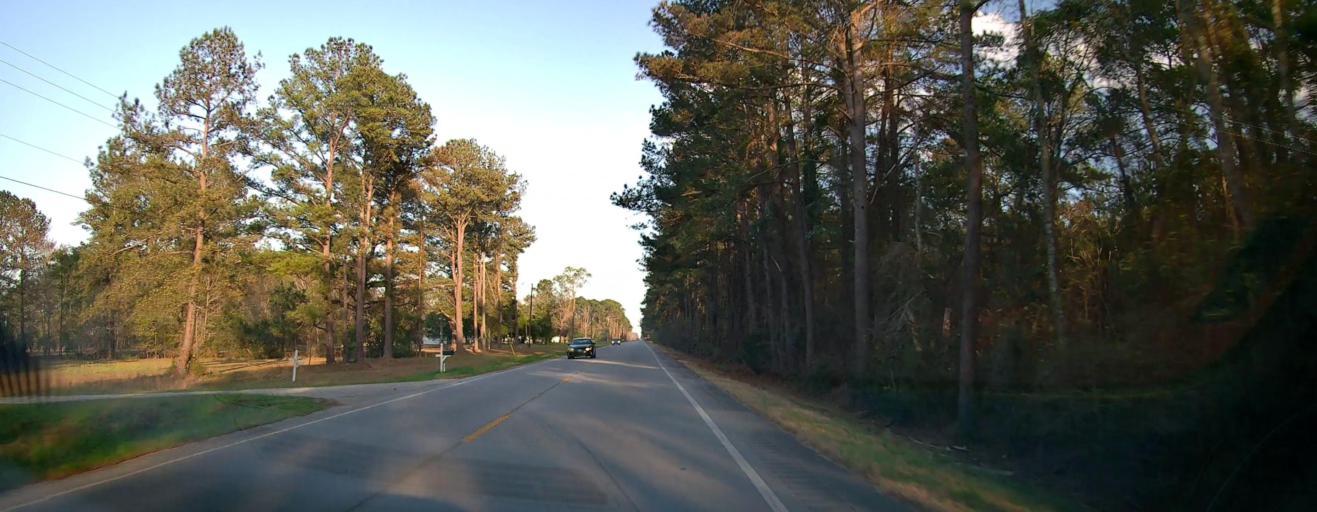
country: US
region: Georgia
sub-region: Bryan County
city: Pembroke
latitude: 32.1415
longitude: -81.7057
